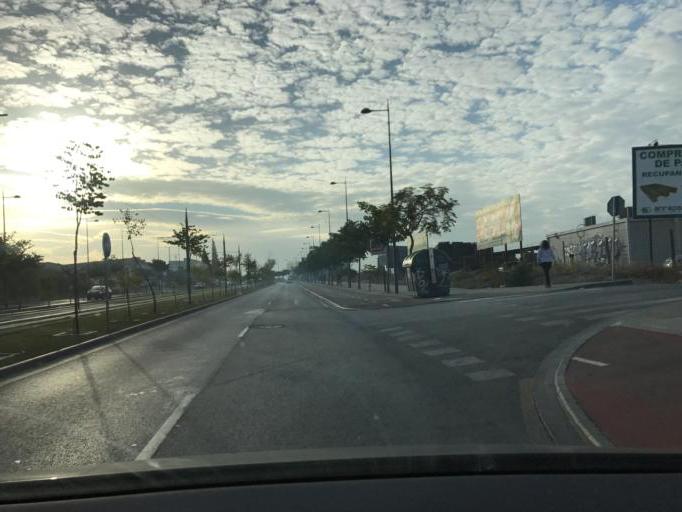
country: ES
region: Andalusia
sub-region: Provincia de Granada
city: Maracena
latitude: 37.2177
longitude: -3.6419
